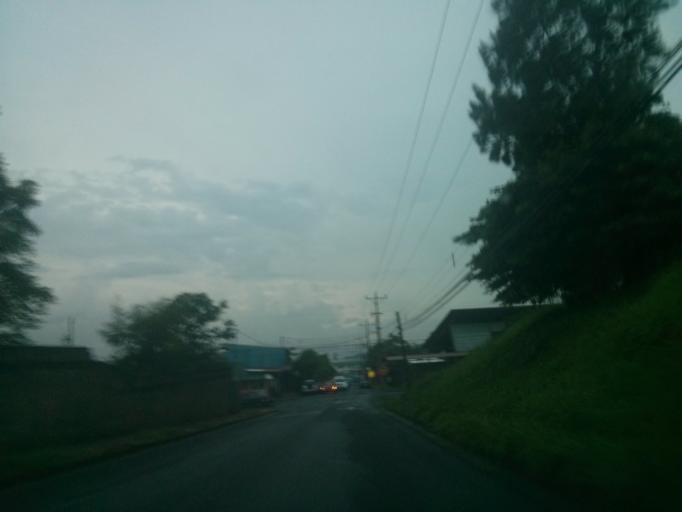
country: CR
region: Alajuela
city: Alajuela
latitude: 10.0086
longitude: -84.2257
